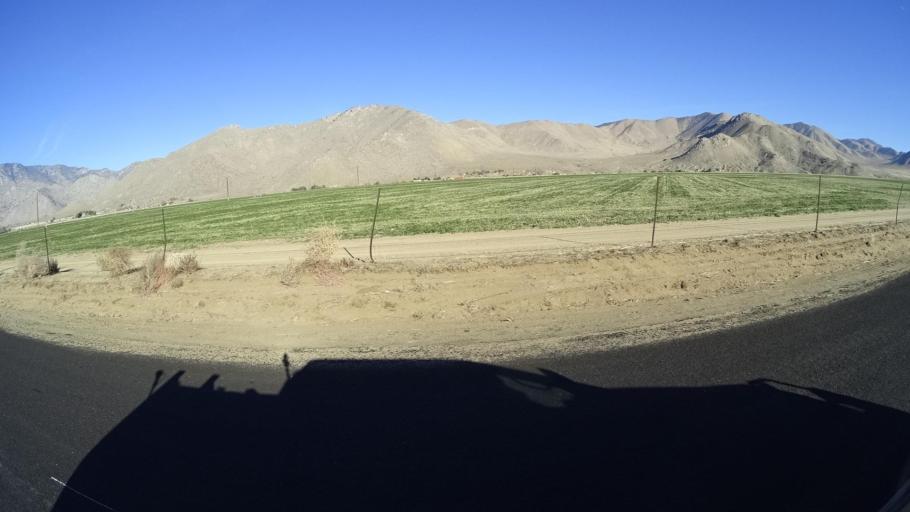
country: US
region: California
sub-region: Kern County
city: Weldon
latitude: 35.6359
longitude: -118.2670
